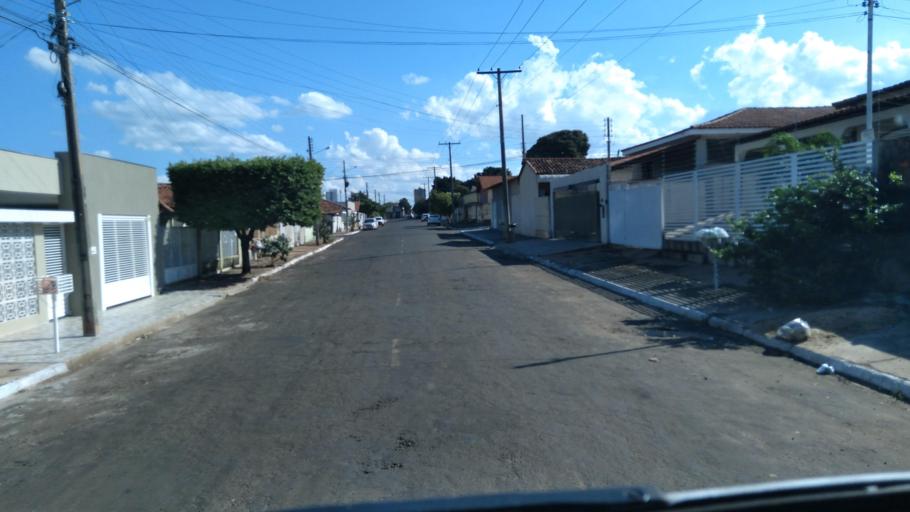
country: BR
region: Goias
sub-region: Mineiros
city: Mineiros
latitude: -17.5604
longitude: -52.5476
